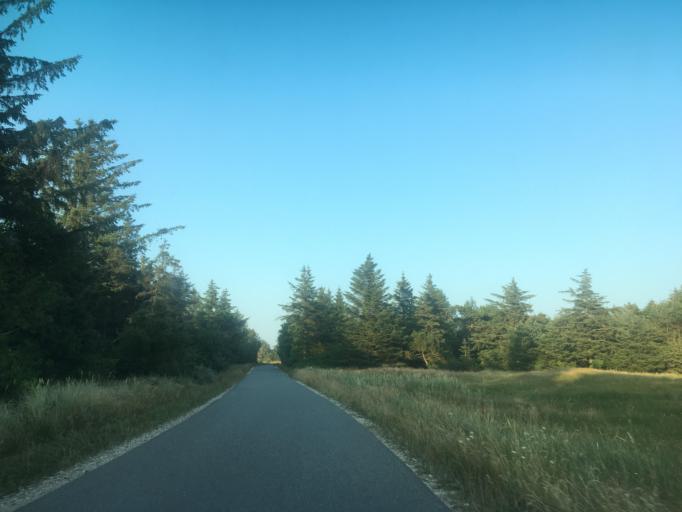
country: DK
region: North Denmark
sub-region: Thisted Kommune
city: Hurup
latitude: 56.8142
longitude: 8.3182
